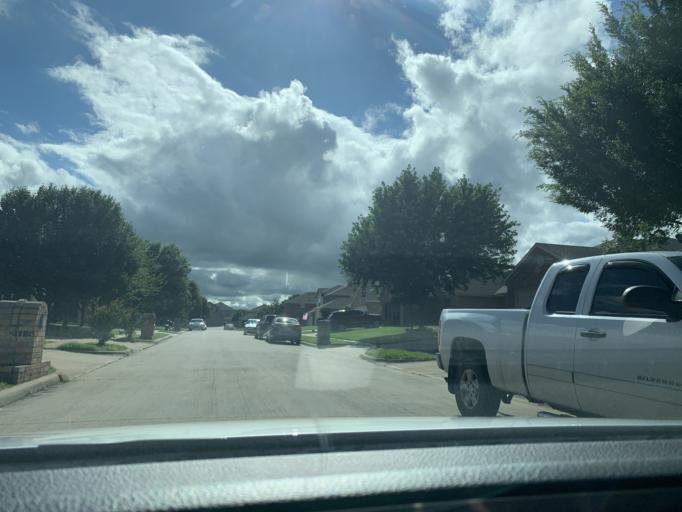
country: US
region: Texas
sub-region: Dallas County
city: Cedar Hill
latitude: 32.6407
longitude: -97.0336
